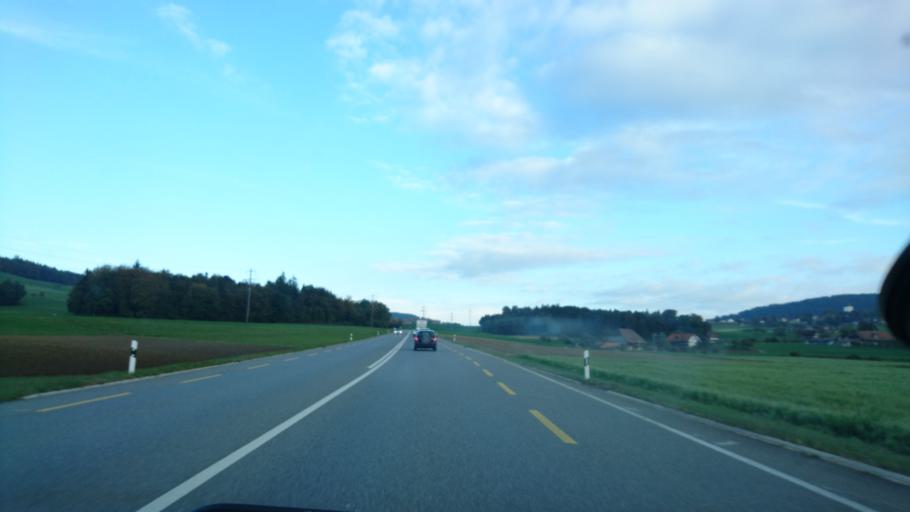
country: CH
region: Bern
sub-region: Bern-Mittelland District
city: Biglen
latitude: 46.9180
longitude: 7.5937
